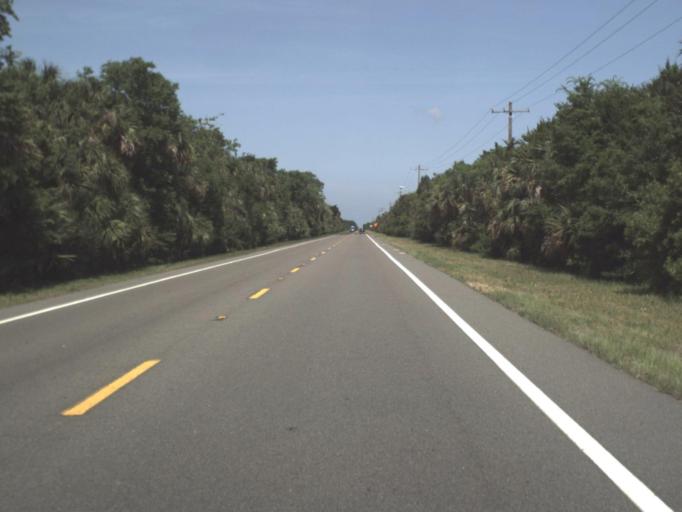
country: US
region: Florida
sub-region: Duval County
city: Atlantic Beach
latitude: 30.3987
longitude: -81.4921
